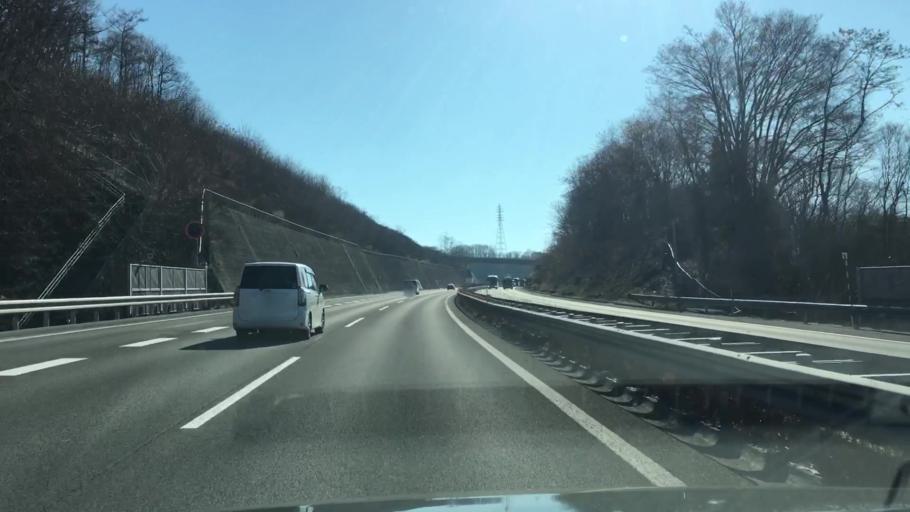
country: JP
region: Nagano
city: Ueda
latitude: 36.4040
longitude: 138.3109
